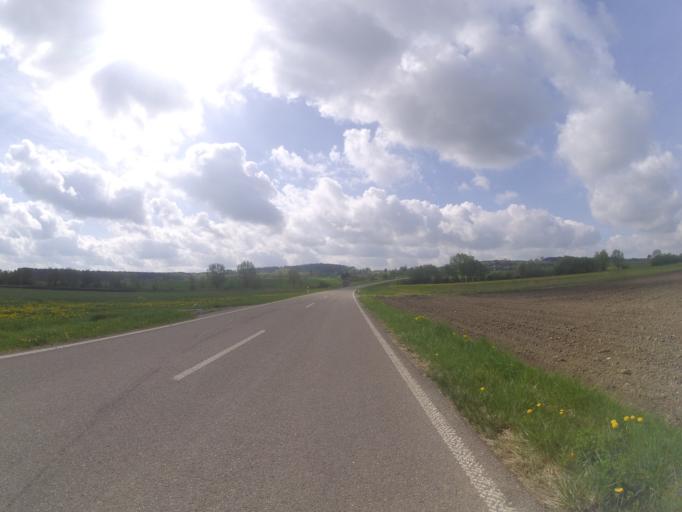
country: DE
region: Baden-Wuerttemberg
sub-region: Tuebingen Region
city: Griesingen
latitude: 48.2377
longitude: 9.7687
